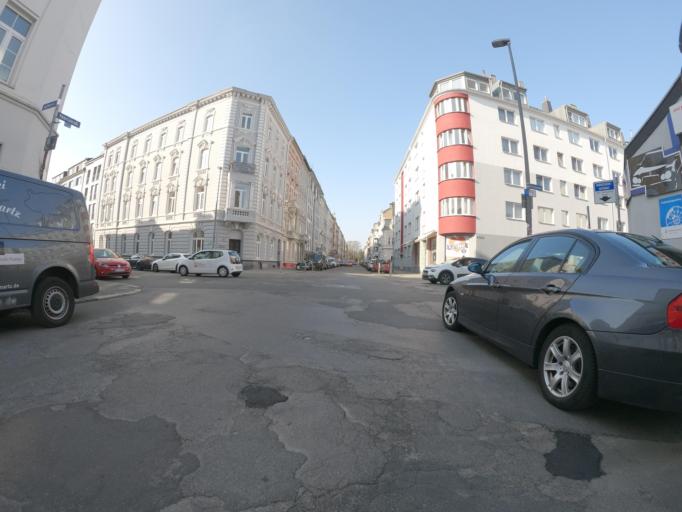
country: DE
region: North Rhine-Westphalia
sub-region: Regierungsbezirk Koln
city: Aachen
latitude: 50.7719
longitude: 6.1073
